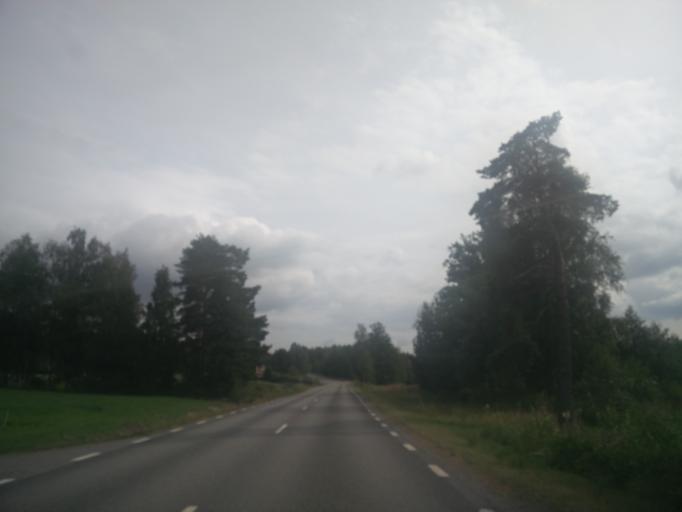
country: SE
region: Vaermland
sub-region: Arvika Kommun
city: Arvika
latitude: 59.7431
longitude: 12.5567
